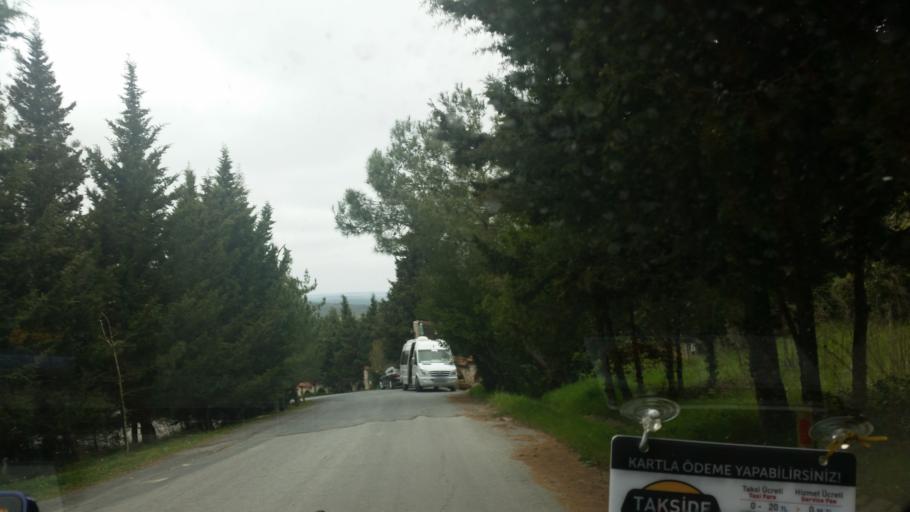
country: TR
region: Istanbul
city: Boyalik
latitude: 41.2880
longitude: 28.6039
